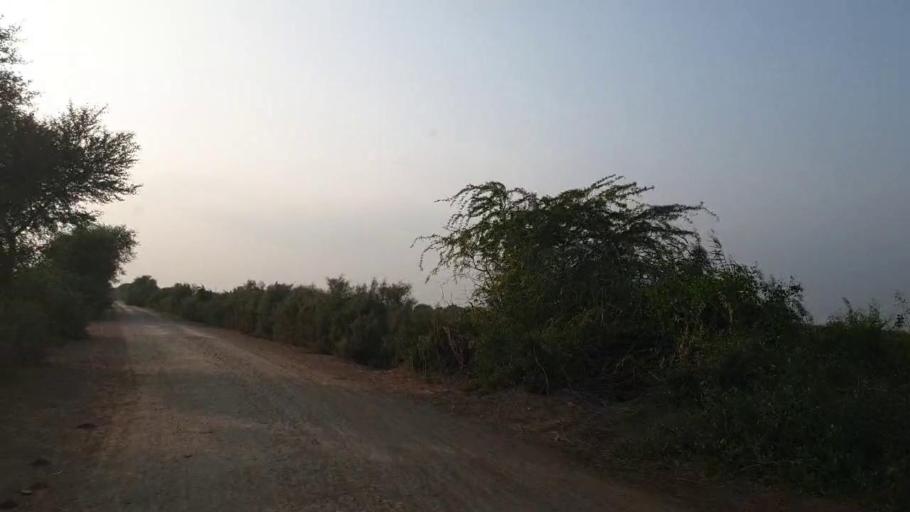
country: PK
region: Sindh
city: Tando Ghulam Ali
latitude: 25.0525
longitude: 68.9644
